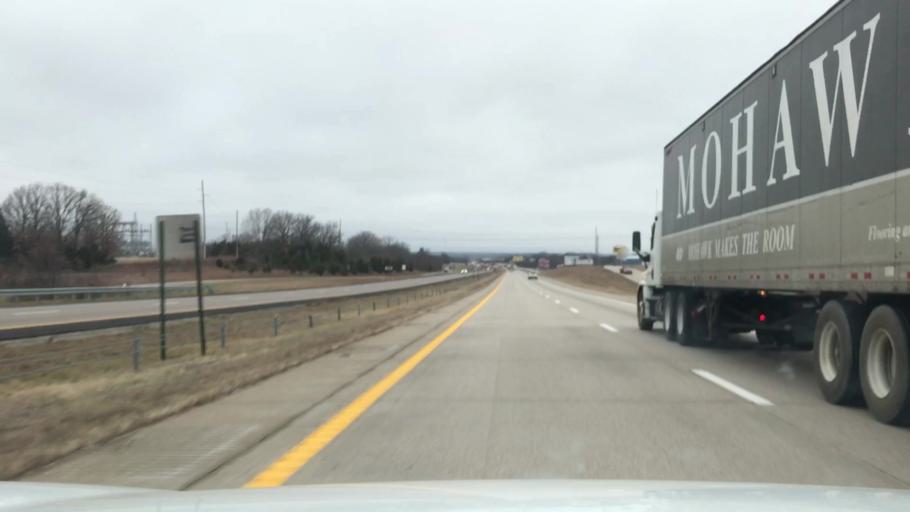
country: US
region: Missouri
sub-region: Franklin County
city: Sullivan
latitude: 38.1831
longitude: -91.2016
